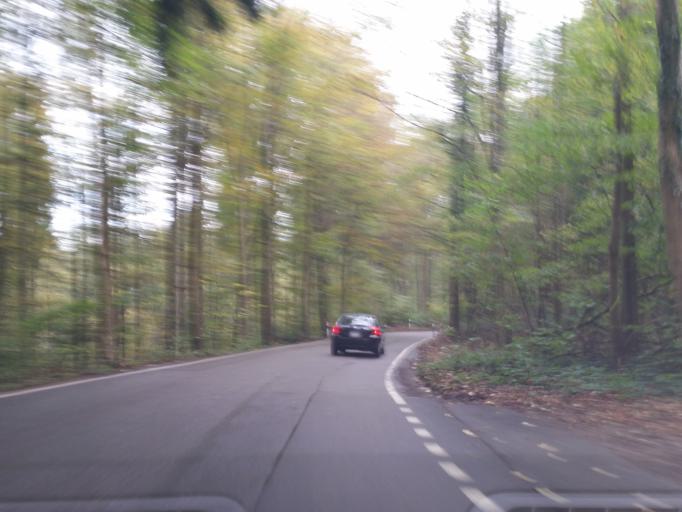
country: CH
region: Zurich
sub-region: Bezirk Uster
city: Gockhausen
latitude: 47.3813
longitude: 8.6097
